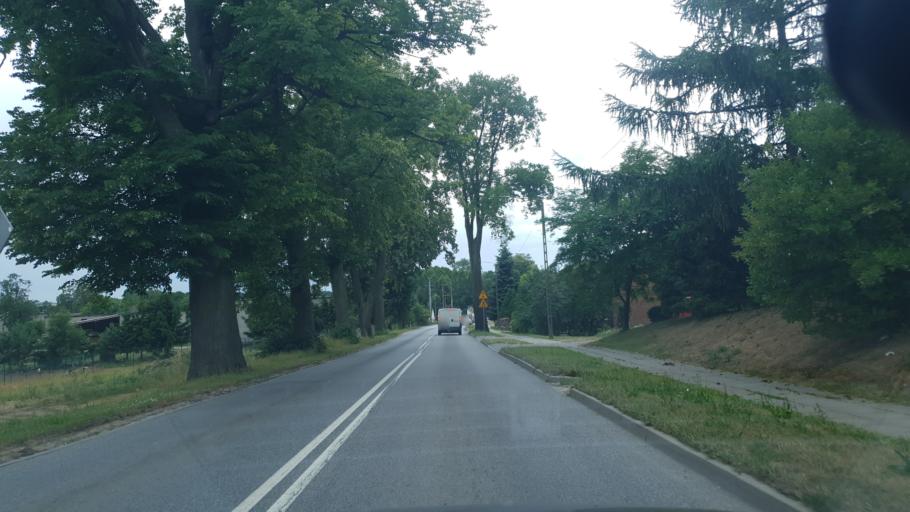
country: PL
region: Pomeranian Voivodeship
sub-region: Powiat kartuski
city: Przodkowo
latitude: 54.3806
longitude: 18.3170
